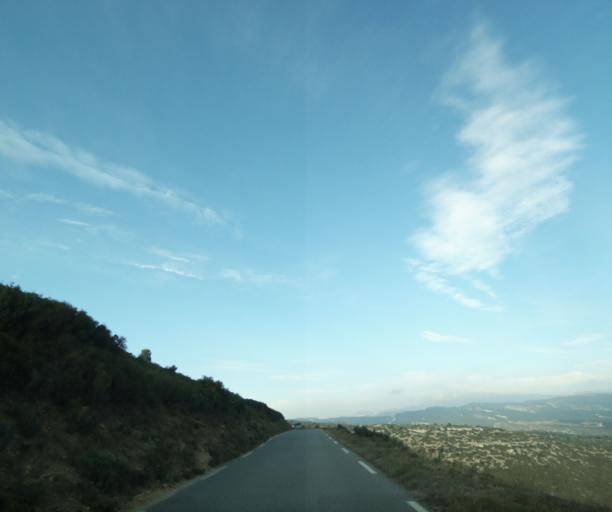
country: FR
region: Provence-Alpes-Cote d'Azur
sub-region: Departement des Bouches-du-Rhone
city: Cassis
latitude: 43.1898
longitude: 5.5586
